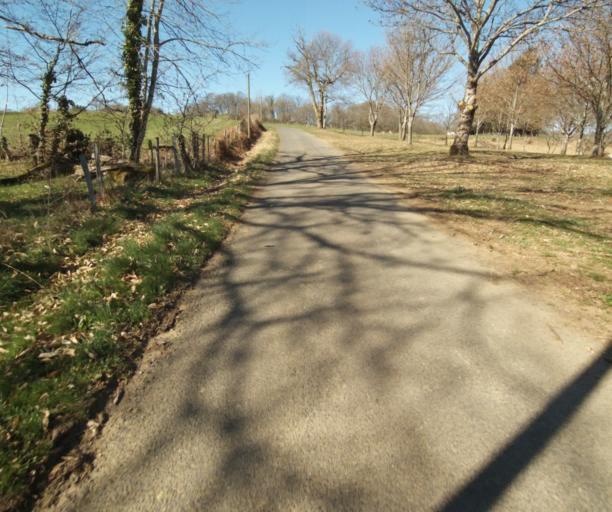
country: FR
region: Limousin
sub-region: Departement de la Correze
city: Seilhac
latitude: 45.3761
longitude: 1.7351
